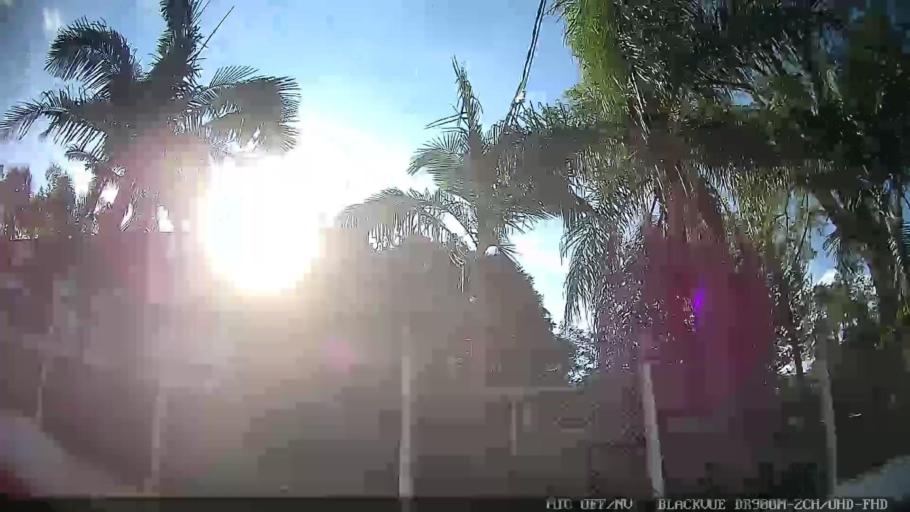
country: BR
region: Sao Paulo
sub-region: Serra Negra
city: Serra Negra
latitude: -22.6332
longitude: -46.6989
